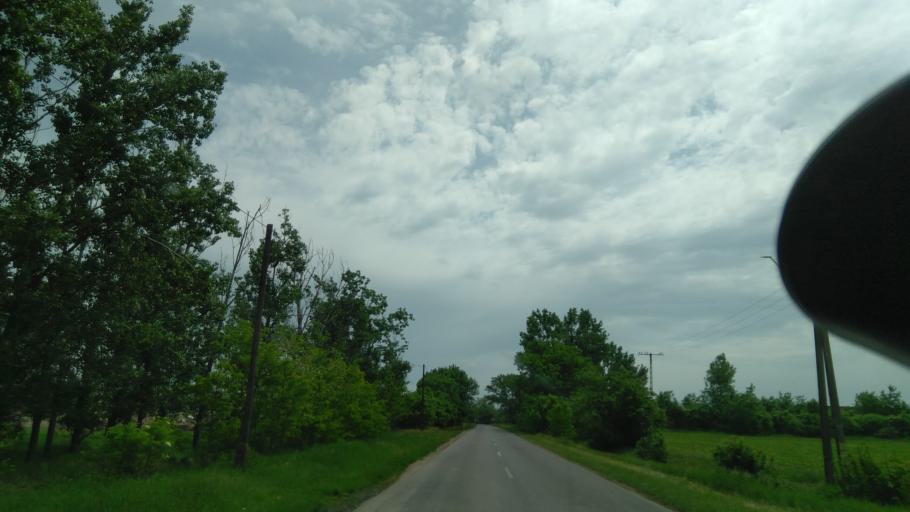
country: HU
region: Bekes
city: Fuzesgyarmat
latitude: 47.0992
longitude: 21.2268
